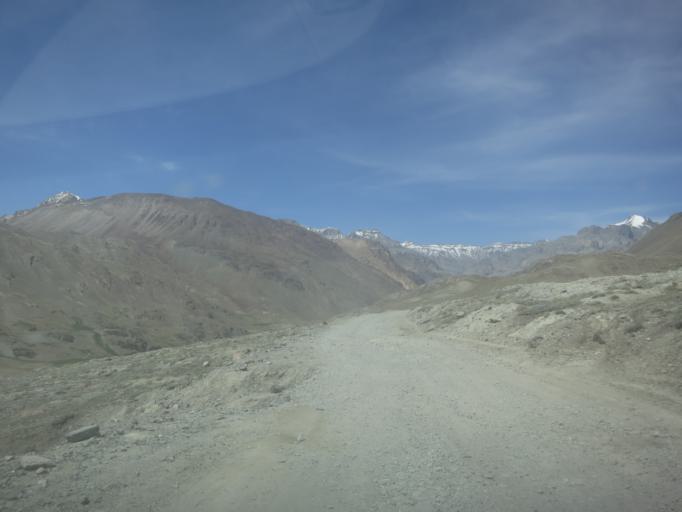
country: IN
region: Himachal Pradesh
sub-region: Kulu
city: Manali
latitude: 32.3999
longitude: 77.6373
